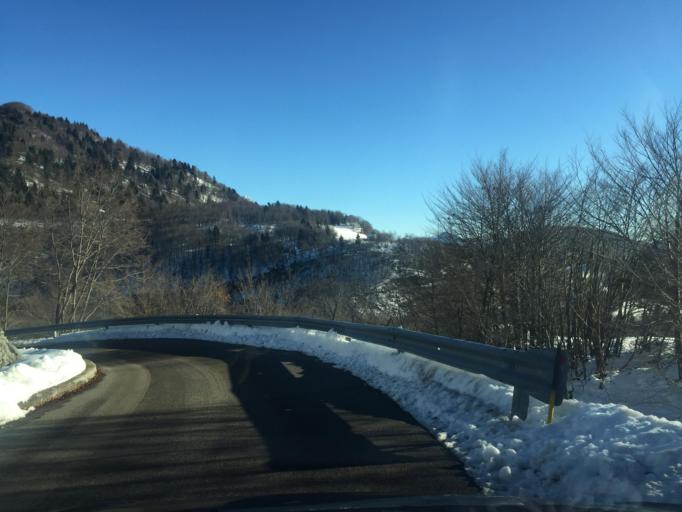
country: IT
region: Friuli Venezia Giulia
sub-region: Provincia di Udine
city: Lauco
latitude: 46.4364
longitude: 12.9644
